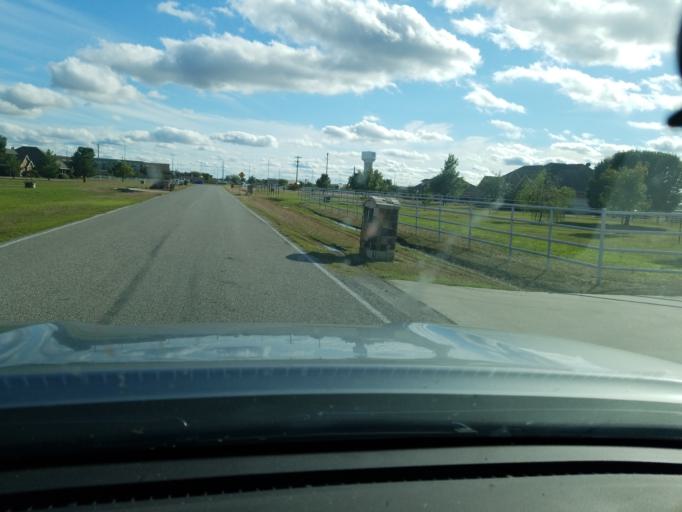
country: US
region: Texas
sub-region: Tarrant County
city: Pecan Acres
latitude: 32.9706
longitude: -97.4123
